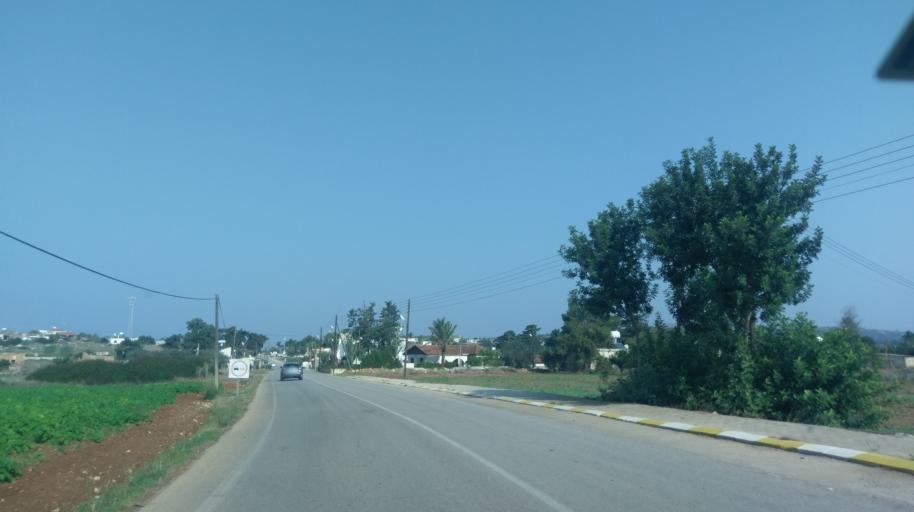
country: CY
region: Ammochostos
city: Leonarisso
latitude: 35.4994
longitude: 34.1601
